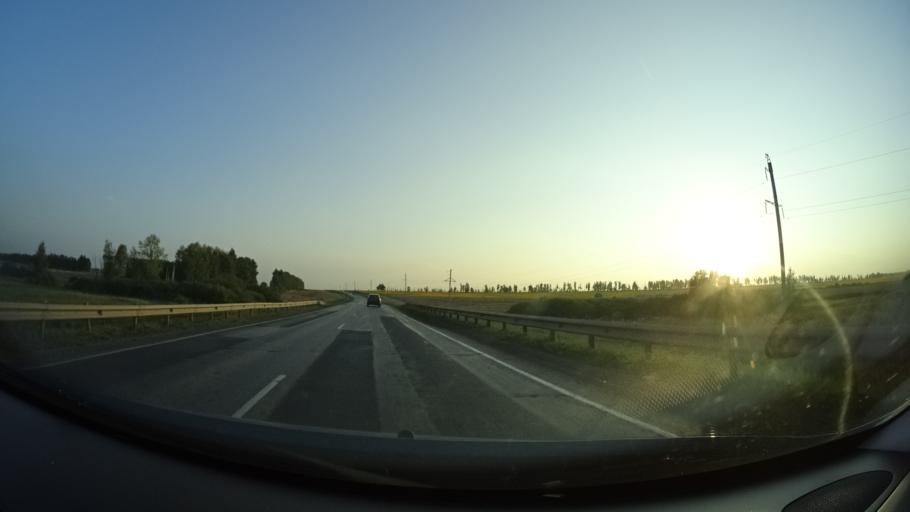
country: RU
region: Samara
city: Sernovodsk
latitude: 53.9535
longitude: 51.3854
